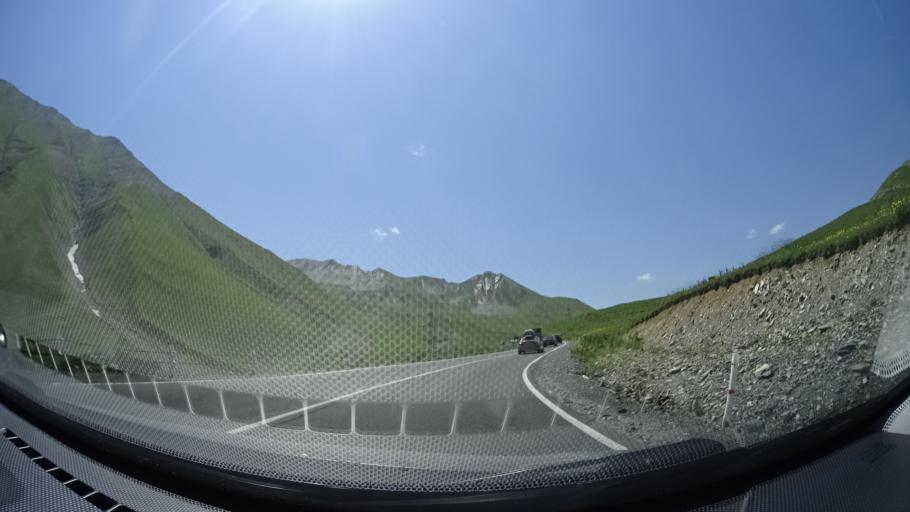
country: GE
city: Gudauri
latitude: 42.5216
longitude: 44.4674
